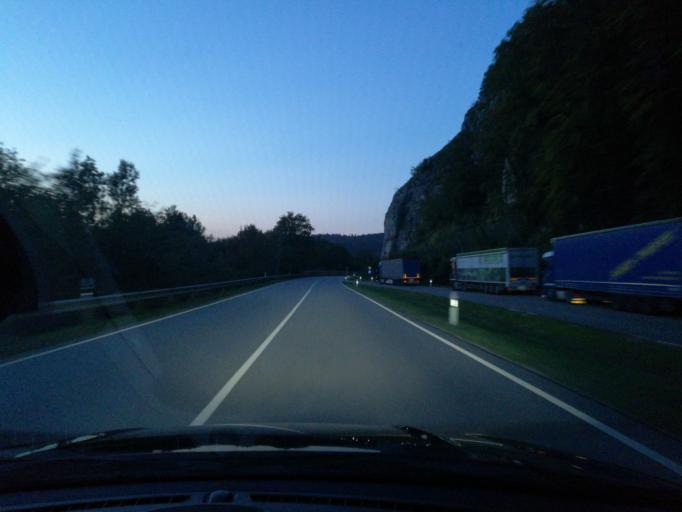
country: DE
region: Bavaria
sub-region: Lower Bavaria
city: Saal
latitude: 48.9109
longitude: 11.9722
